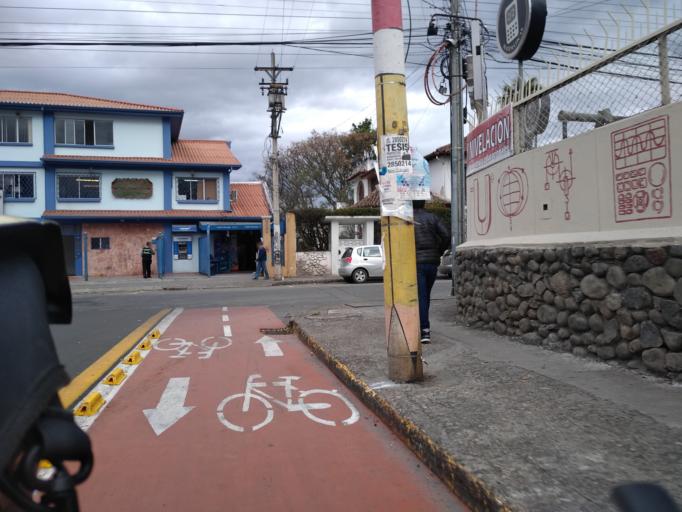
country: EC
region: Azuay
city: Cuenca
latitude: -2.9048
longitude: -79.0048
